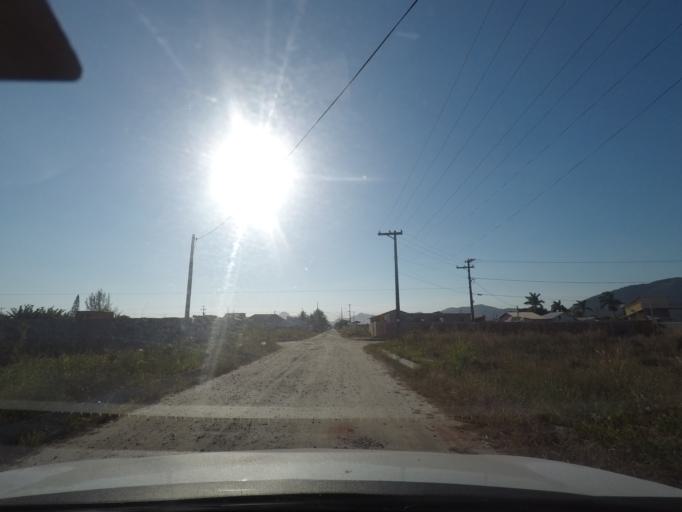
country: BR
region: Rio de Janeiro
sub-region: Marica
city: Marica
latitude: -22.9619
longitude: -42.9358
